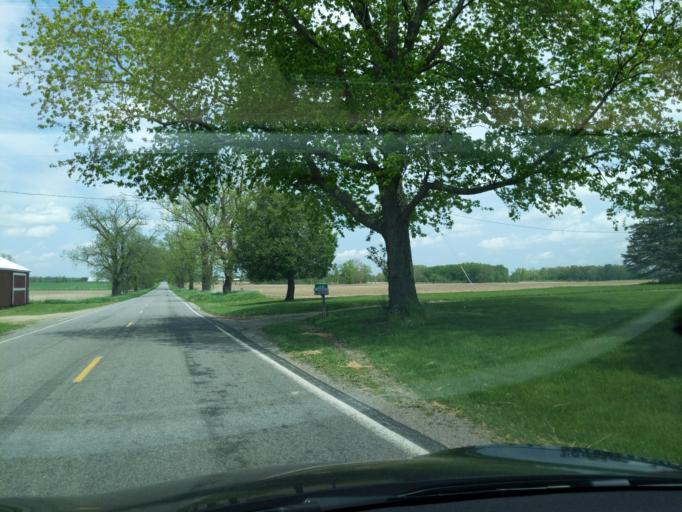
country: US
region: Michigan
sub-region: Ingham County
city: Stockbridge
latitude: 42.4728
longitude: -84.1603
